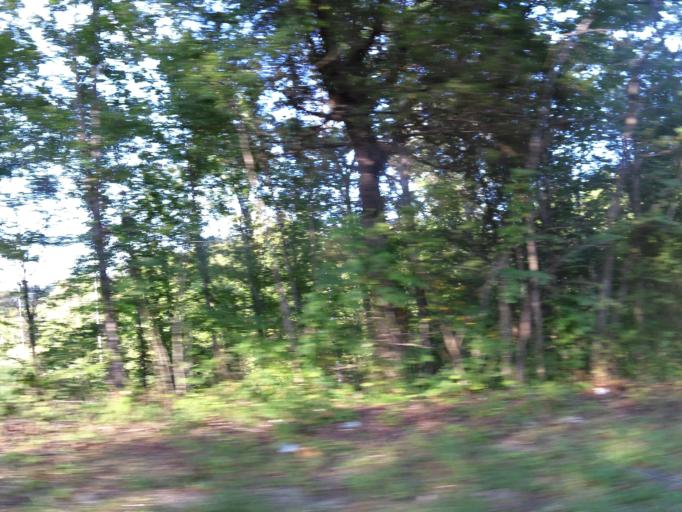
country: US
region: Tennessee
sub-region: Union County
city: Condon
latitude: 36.1942
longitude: -83.8281
